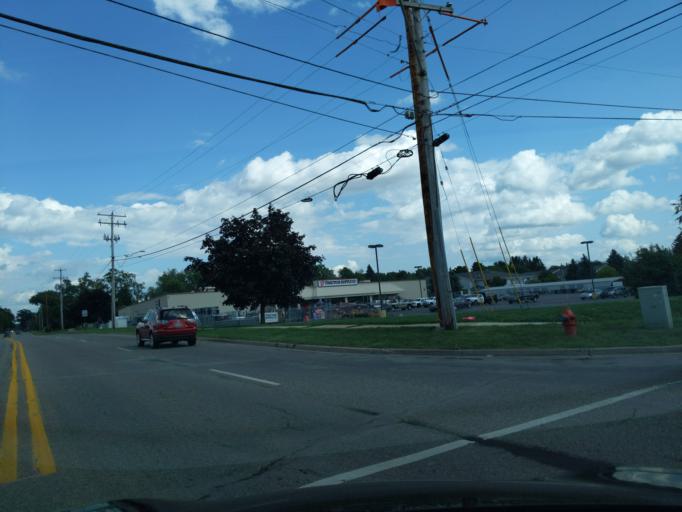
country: US
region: Michigan
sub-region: Jackson County
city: Jackson
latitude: 42.2765
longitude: -84.4532
